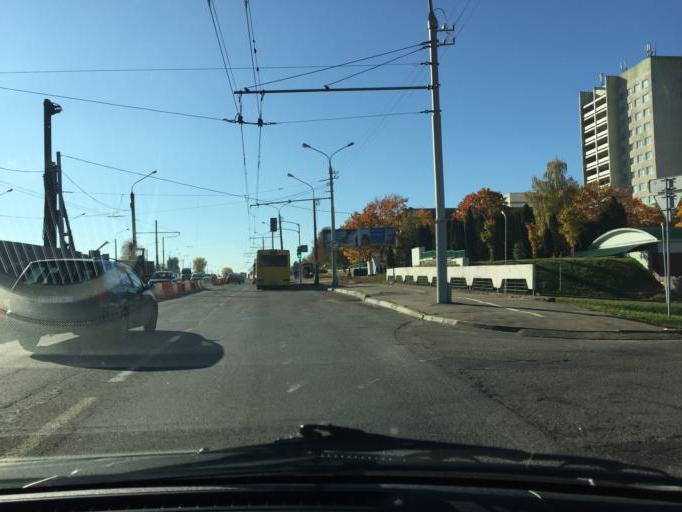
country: BY
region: Minsk
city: Syenitsa
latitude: 53.8532
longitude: 27.5378
